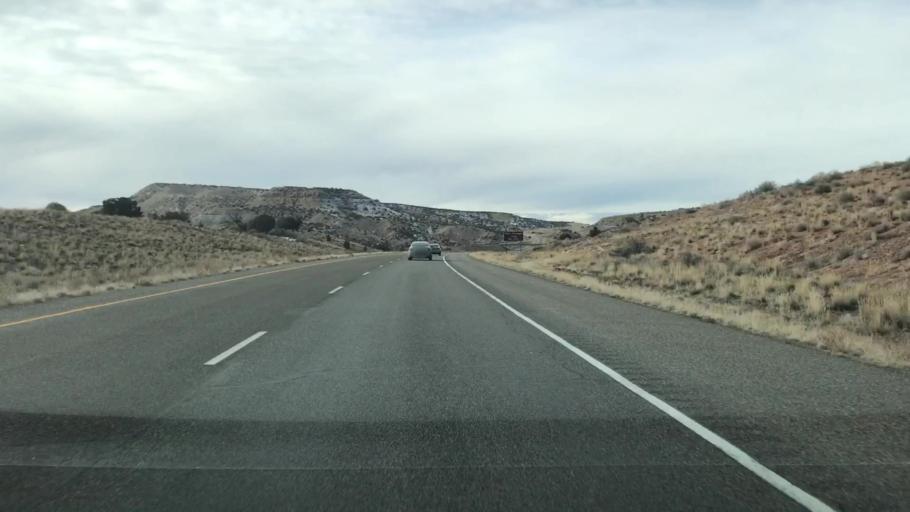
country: US
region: Colorado
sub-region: Mesa County
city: Loma
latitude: 39.1931
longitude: -109.0073
